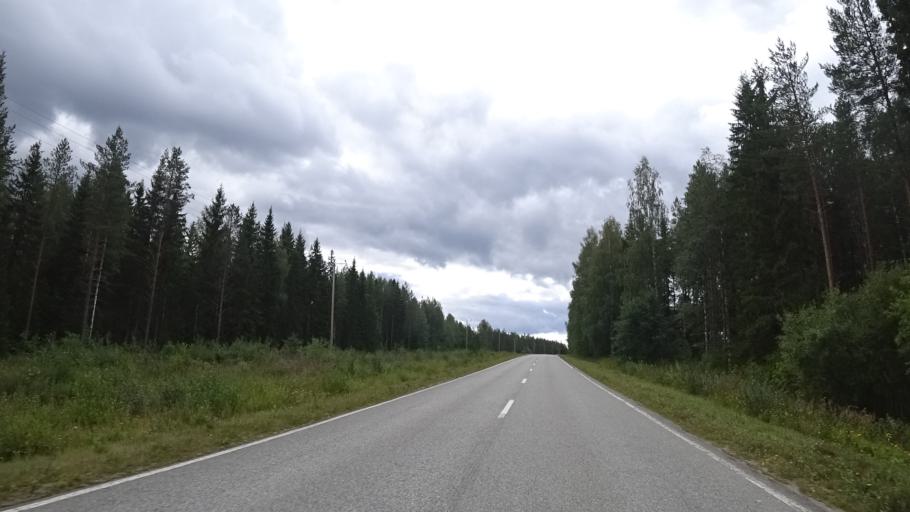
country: FI
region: North Karelia
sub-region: Joensuu
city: Ilomantsi
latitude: 62.6365
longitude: 31.2831
